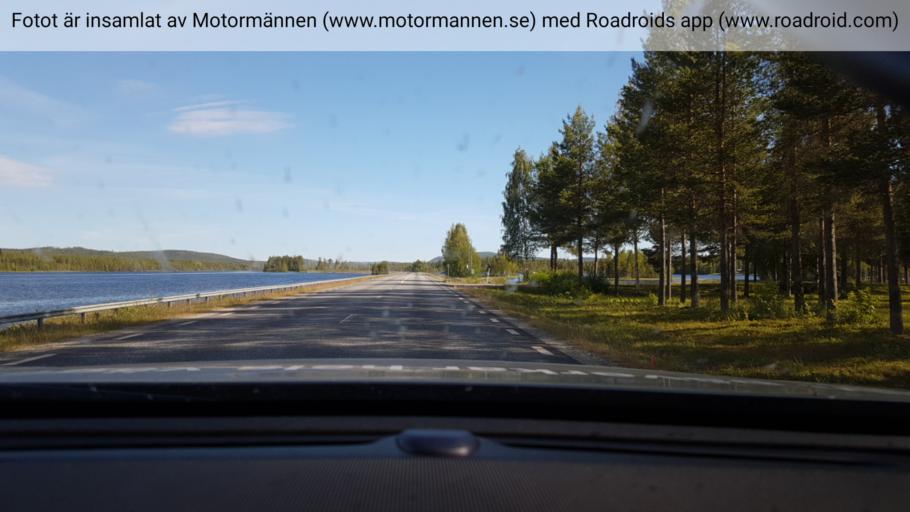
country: SE
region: Vaesterbotten
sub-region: Lycksele Kommun
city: Soderfors
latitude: 64.7580
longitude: 18.1670
